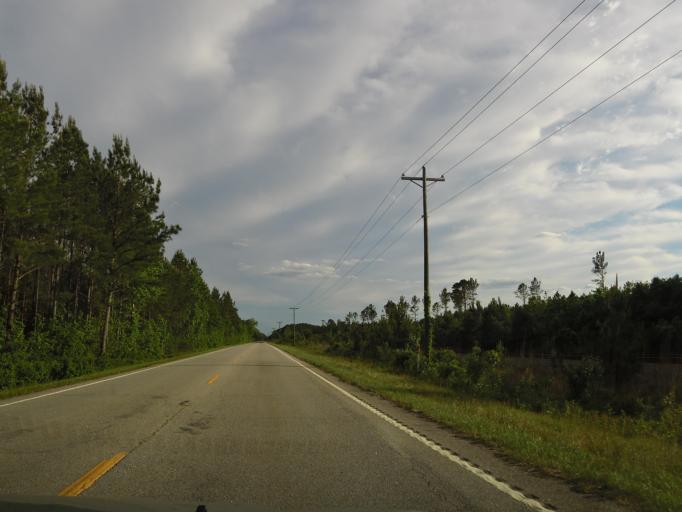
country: US
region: South Carolina
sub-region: Hampton County
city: Estill
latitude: 32.6259
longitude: -81.2444
